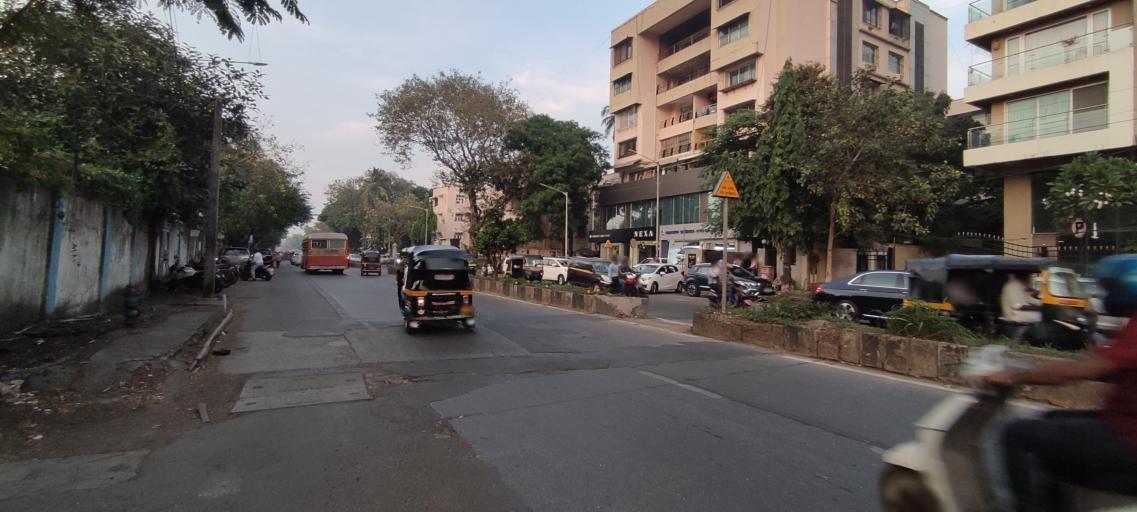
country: IN
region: Maharashtra
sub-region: Mumbai Suburban
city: Mumbai
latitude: 19.0945
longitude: 72.8396
